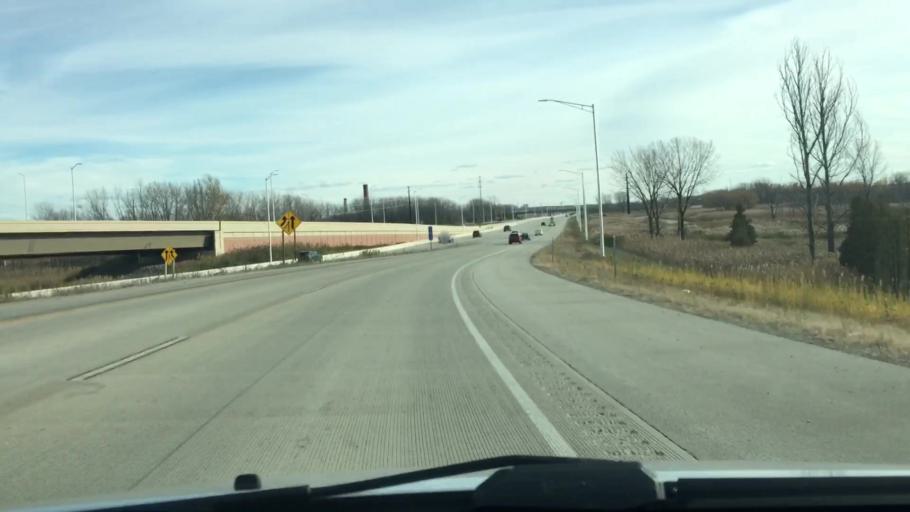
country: US
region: Wisconsin
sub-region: Brown County
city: Howard
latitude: 44.5581
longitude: -88.0507
